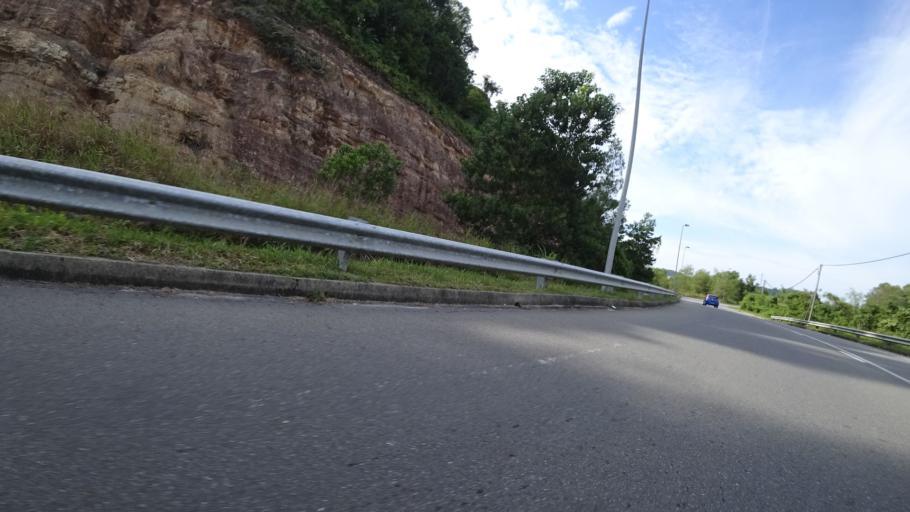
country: BN
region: Brunei and Muara
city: Bandar Seri Begawan
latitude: 4.8853
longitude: 114.8032
